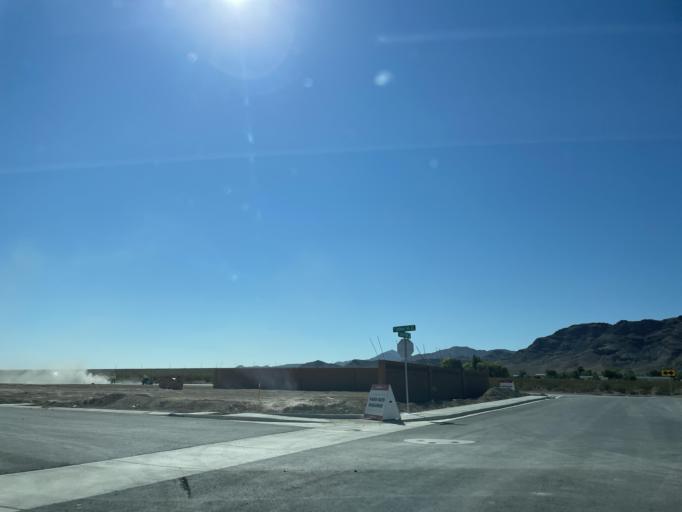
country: US
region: Nevada
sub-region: Nye County
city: Pahrump
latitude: 36.5739
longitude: -115.6633
